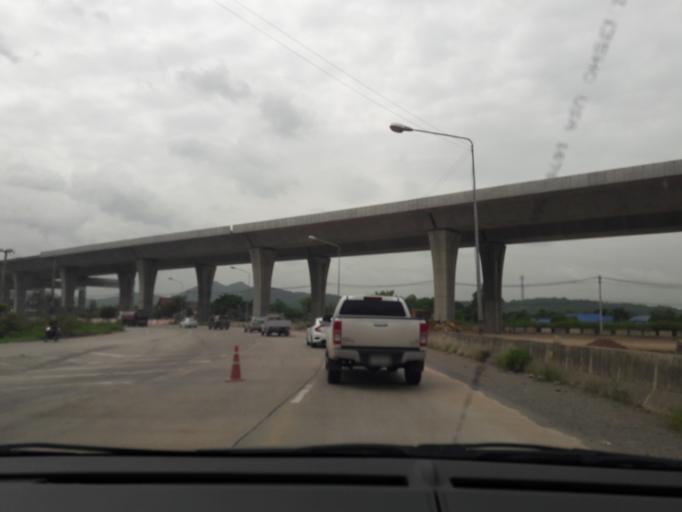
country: TH
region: Sara Buri
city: Saraburi
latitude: 14.4586
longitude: 100.9075
